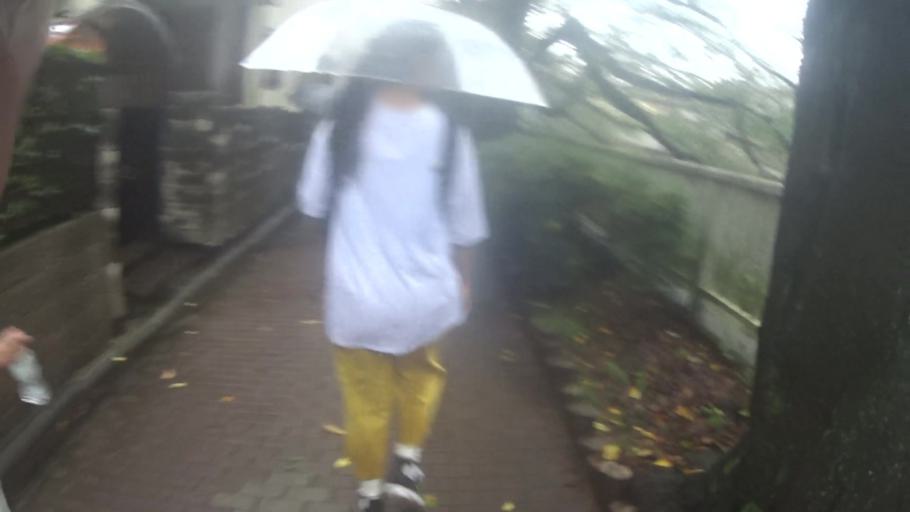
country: JP
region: Saitama
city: Wako
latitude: 35.7491
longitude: 139.6611
